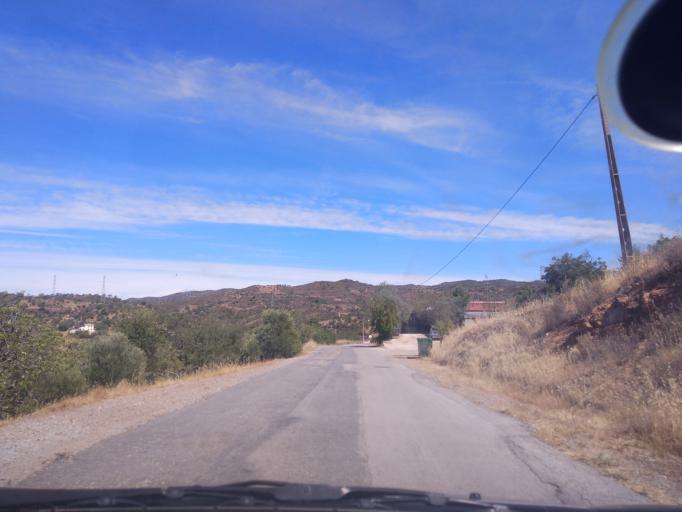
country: PT
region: Faro
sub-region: Sao Bras de Alportel
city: Sao Bras de Alportel
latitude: 37.1756
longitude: -7.8067
